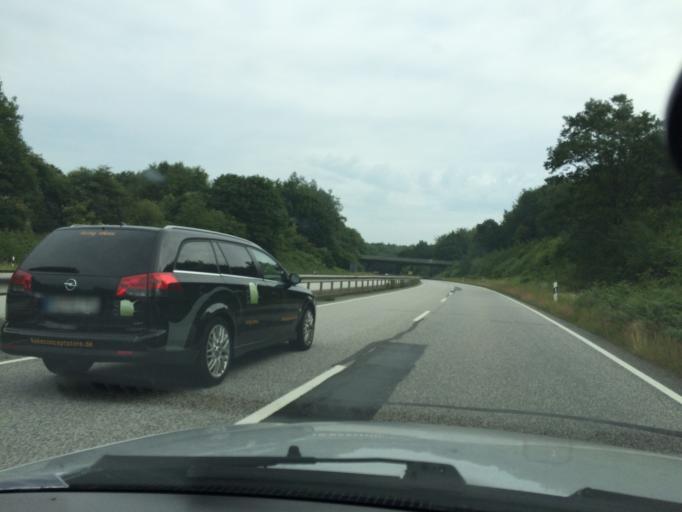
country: DE
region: Schleswig-Holstein
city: Harrislee
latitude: 54.8159
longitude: 9.4146
